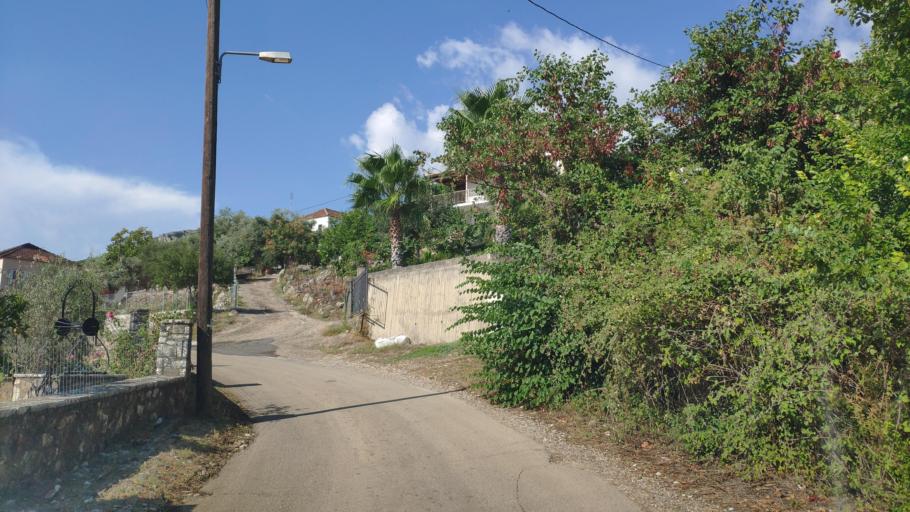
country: GR
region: West Greece
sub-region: Nomos Aitolias kai Akarnanias
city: Fitiai
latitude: 38.6586
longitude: 21.1479
